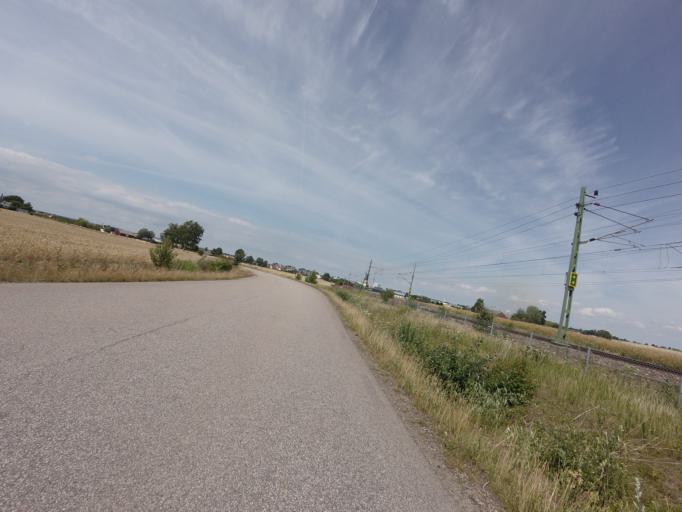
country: SE
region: Skane
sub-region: Helsingborg
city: Rydeback
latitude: 55.9580
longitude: 12.7902
